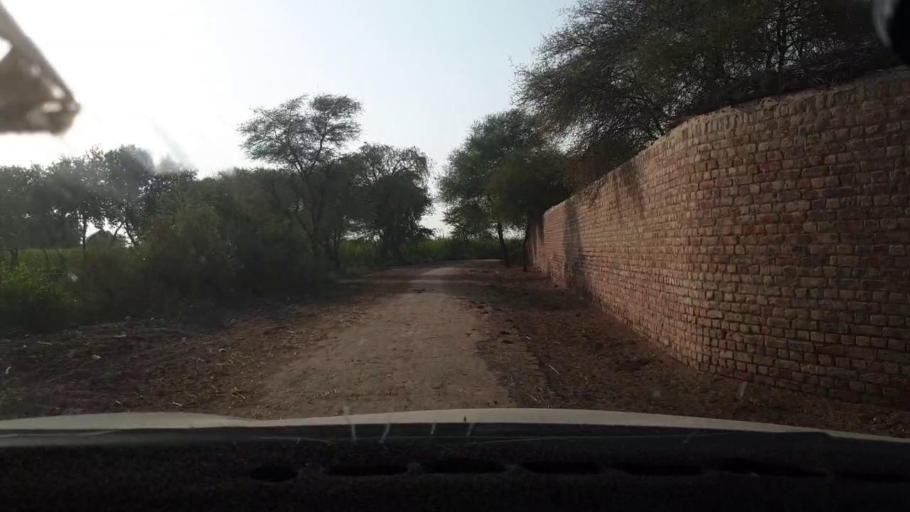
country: PK
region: Sindh
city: Berani
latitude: 25.8187
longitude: 68.7945
